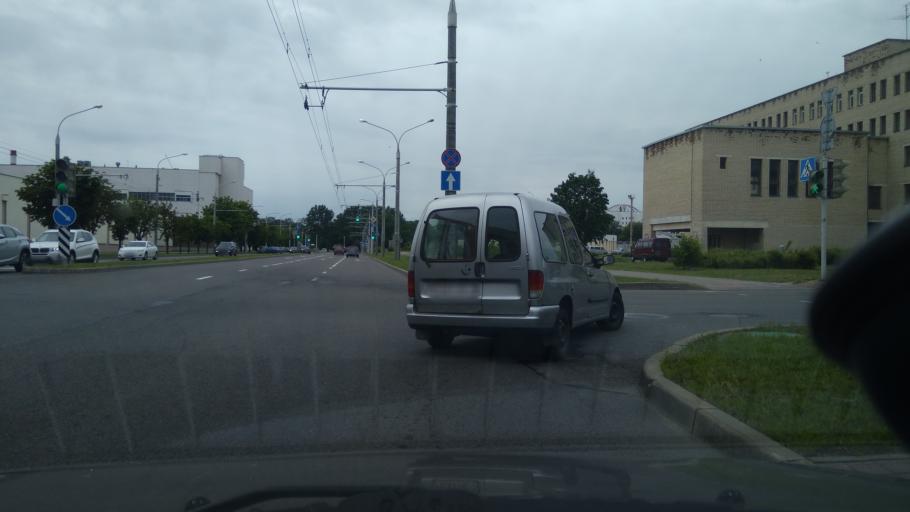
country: BY
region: Minsk
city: Minsk
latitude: 53.9229
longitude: 27.5188
